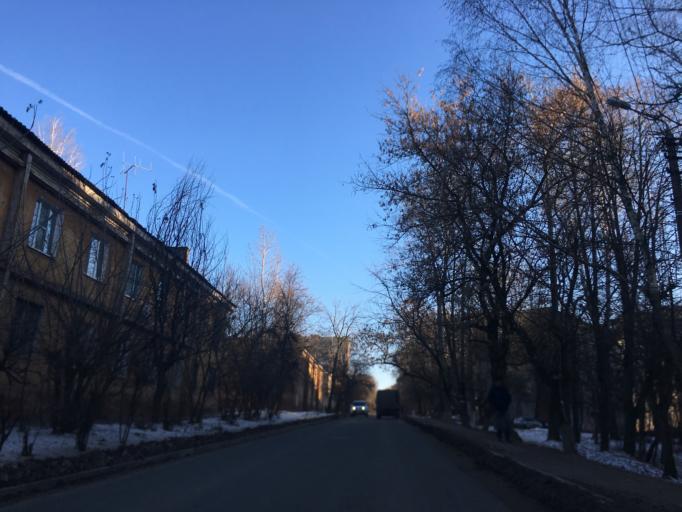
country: RU
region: Tula
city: Mendeleyevskiy
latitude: 54.1676
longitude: 37.5722
